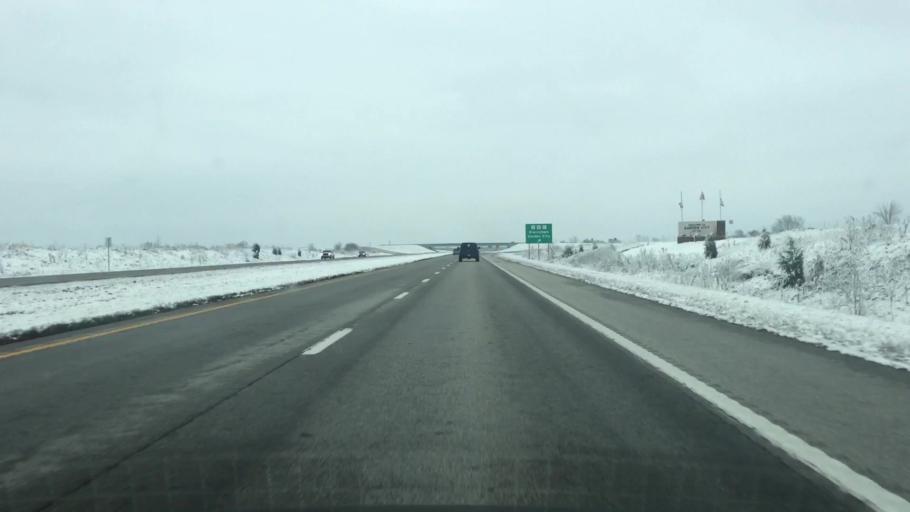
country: US
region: Missouri
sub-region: Cass County
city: Garden City
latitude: 38.5758
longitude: -94.2024
